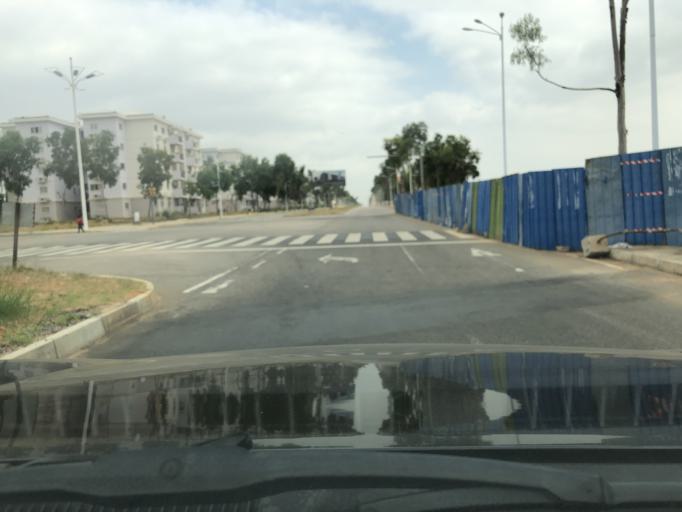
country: AO
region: Luanda
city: Luanda
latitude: -8.9912
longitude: 13.2811
